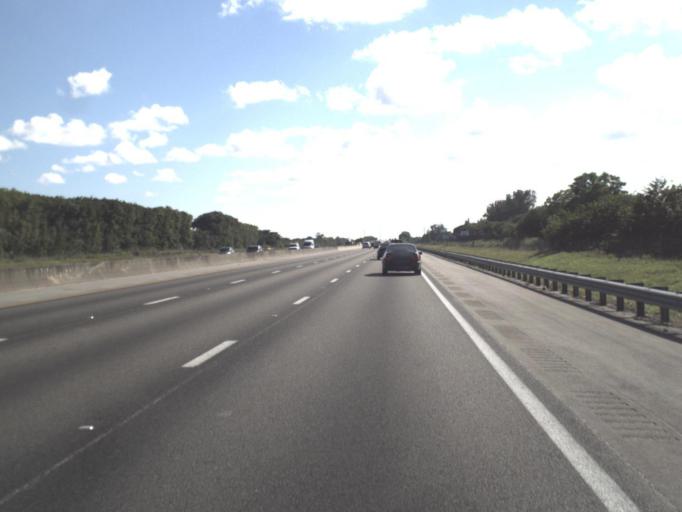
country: US
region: Florida
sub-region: Palm Beach County
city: Kings Point
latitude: 26.4213
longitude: -80.1718
